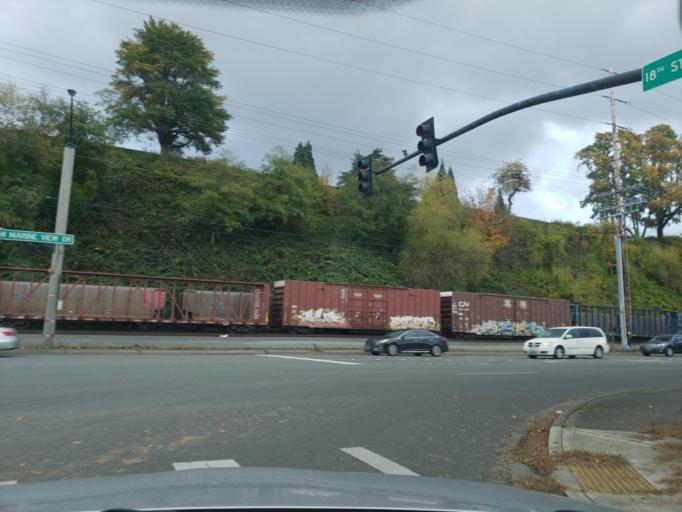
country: US
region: Washington
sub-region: Snohomish County
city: Everett
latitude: 47.9941
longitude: -122.2140
